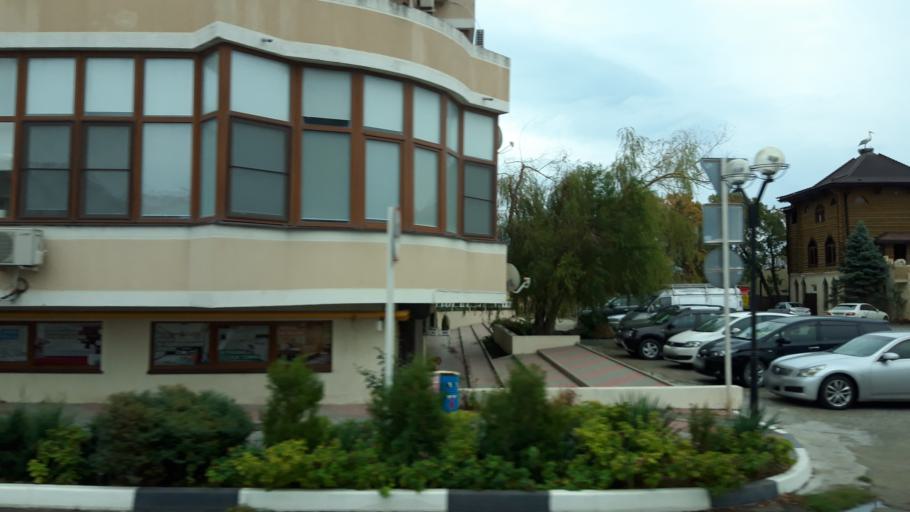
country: RU
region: Krasnodarskiy
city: Gelendzhik
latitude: 44.5474
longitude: 38.0586
